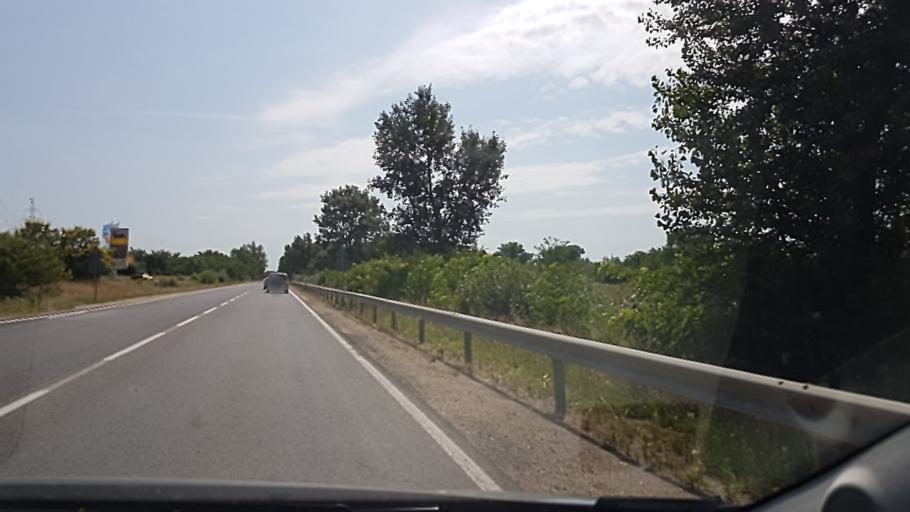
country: HU
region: Pest
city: Dunaharaszti
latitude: 47.3346
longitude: 19.1071
